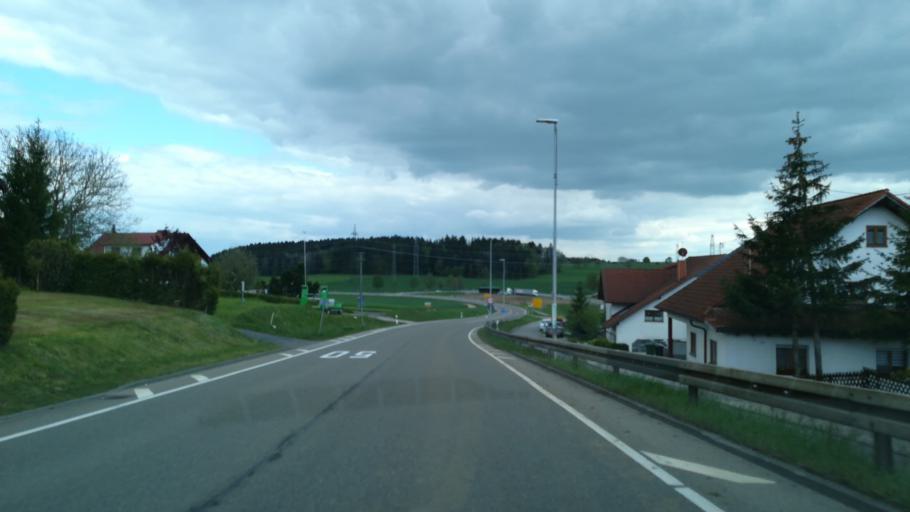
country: DE
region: Baden-Wuerttemberg
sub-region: Freiburg Region
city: Blumberg
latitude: 47.8192
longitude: 8.5769
